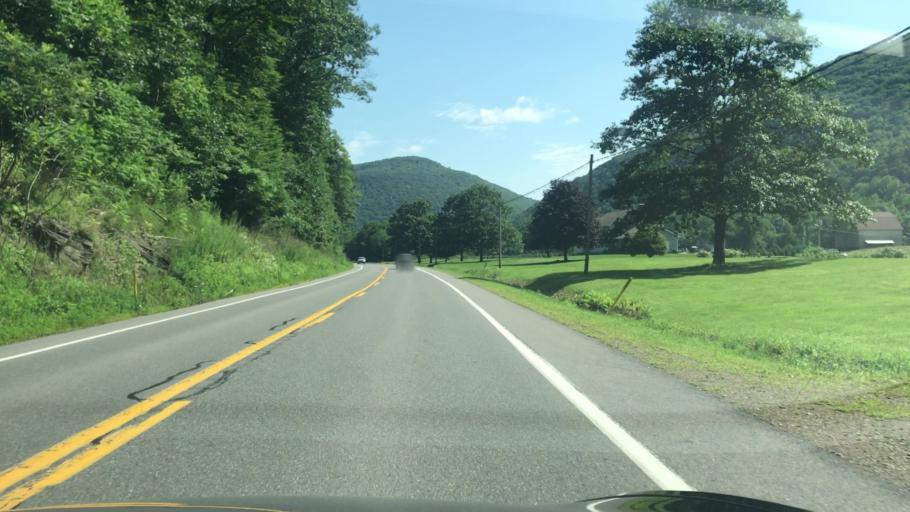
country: US
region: Pennsylvania
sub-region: Bradford County
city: Canton
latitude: 41.4909
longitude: -76.9651
